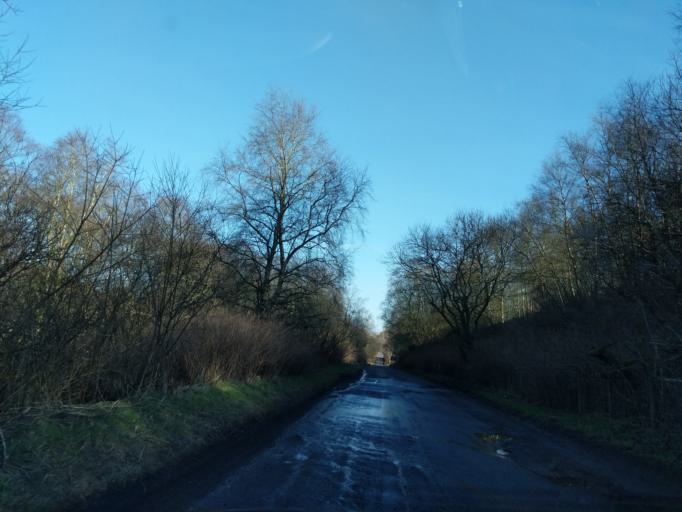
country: GB
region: Scotland
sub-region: The Scottish Borders
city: West Linton
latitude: 55.7199
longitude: -3.4306
